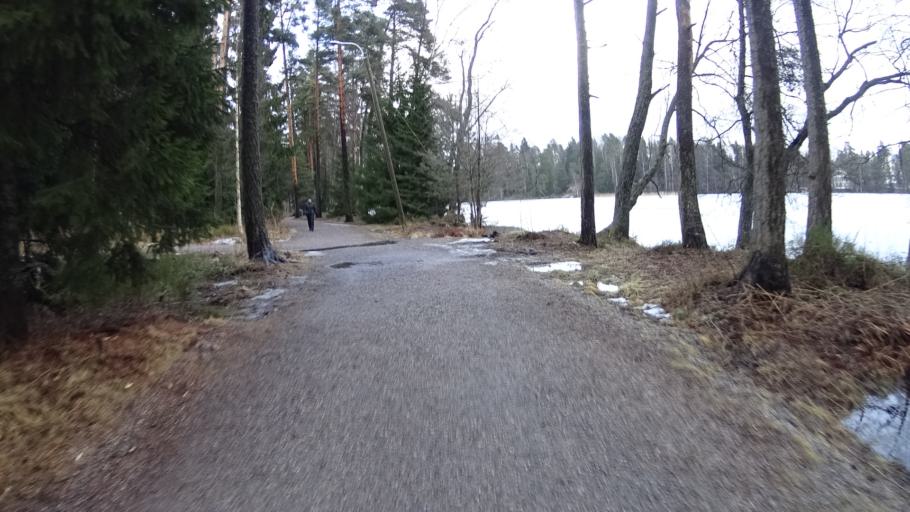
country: FI
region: Uusimaa
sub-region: Helsinki
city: Kauniainen
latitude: 60.2191
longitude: 24.7286
